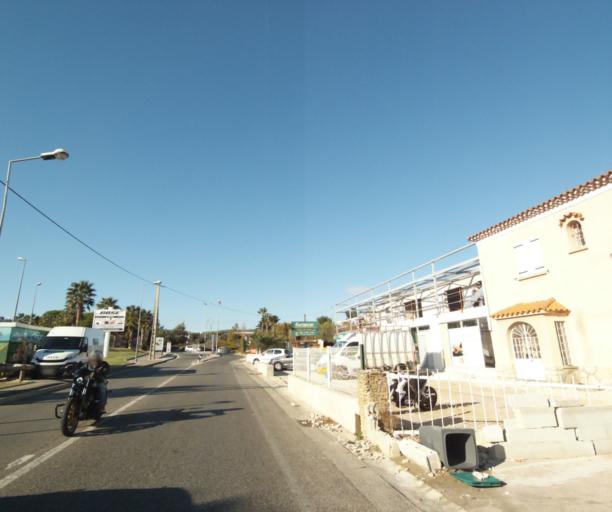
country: FR
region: Provence-Alpes-Cote d'Azur
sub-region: Departement des Bouches-du-Rhone
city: La Ciotat
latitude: 43.1888
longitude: 5.6047
